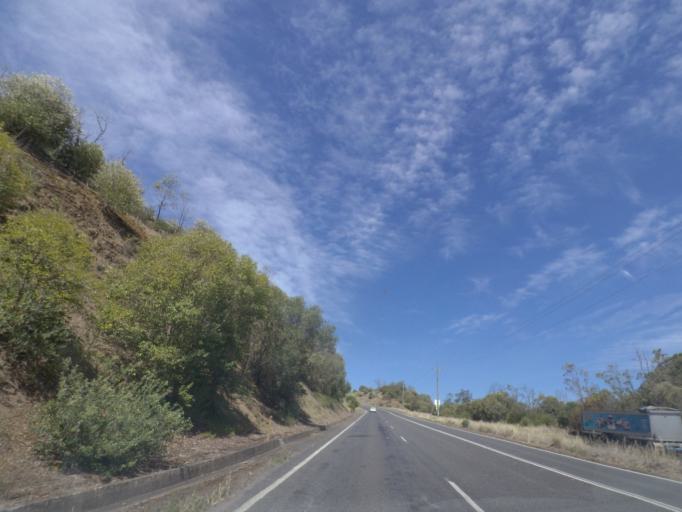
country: AU
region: New South Wales
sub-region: Wollondilly
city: Picton
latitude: -34.1535
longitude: 150.6620
